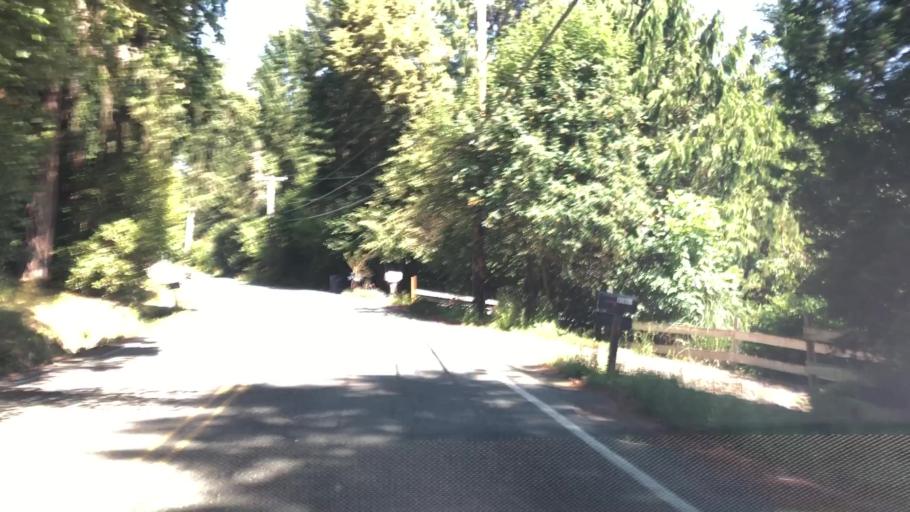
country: US
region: Washington
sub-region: King County
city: Cottage Lake
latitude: 47.7502
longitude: -122.1072
